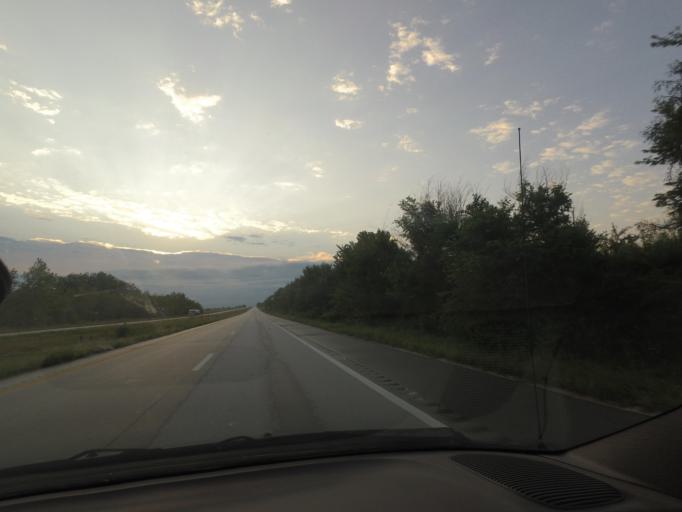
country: US
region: Missouri
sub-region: Shelby County
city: Shelbina
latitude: 39.7324
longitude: -92.2060
